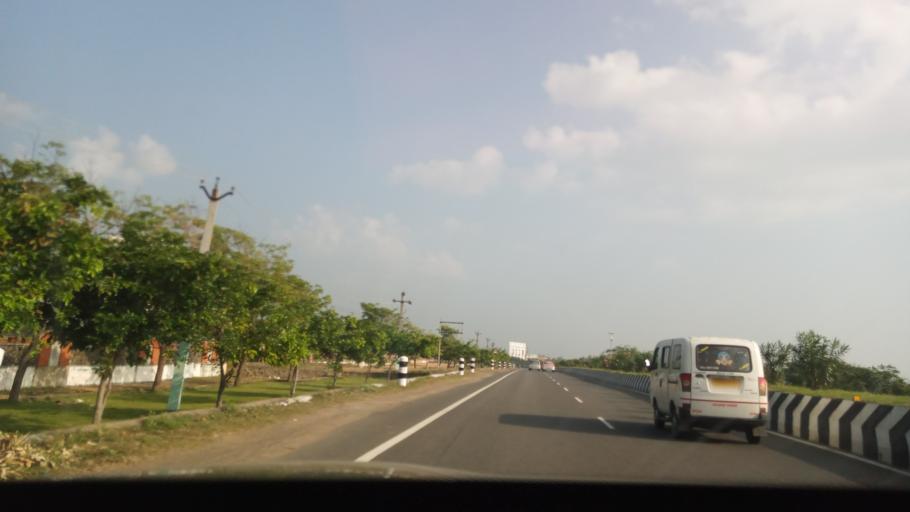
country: IN
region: Tamil Nadu
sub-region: Kancheepuram
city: Injambakkam
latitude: 12.7705
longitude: 80.2481
